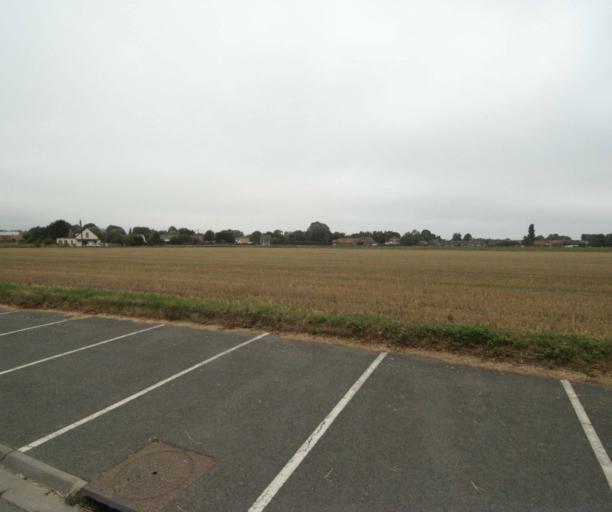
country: FR
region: Nord-Pas-de-Calais
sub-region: Departement du Nord
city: Willems
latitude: 50.6293
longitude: 3.2469
